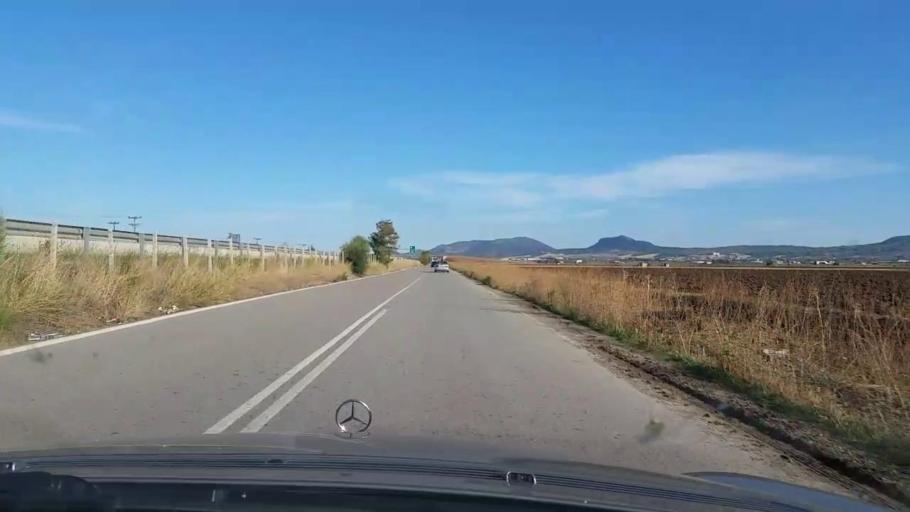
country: GR
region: Central Greece
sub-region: Nomos Voiotias
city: Thivai
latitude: 38.3695
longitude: 23.2918
